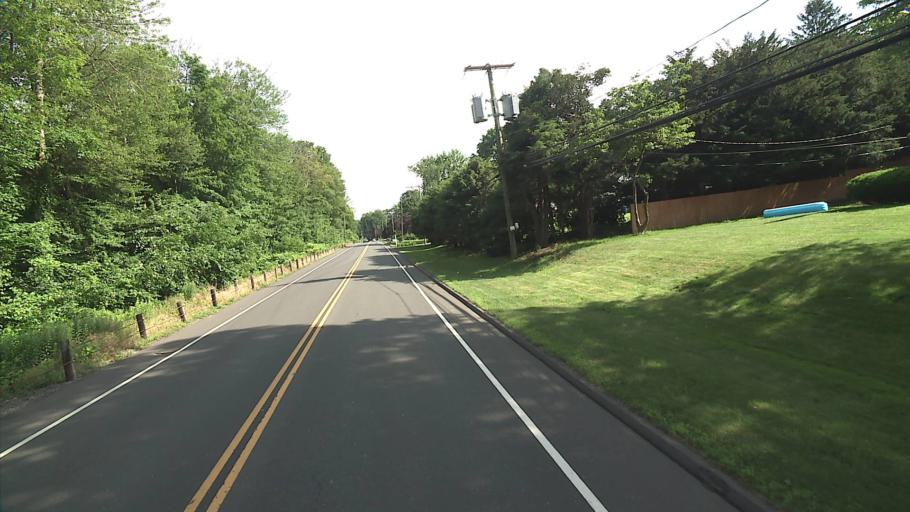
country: US
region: Connecticut
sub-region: New Haven County
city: Waterbury
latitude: 41.5490
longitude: -73.0914
